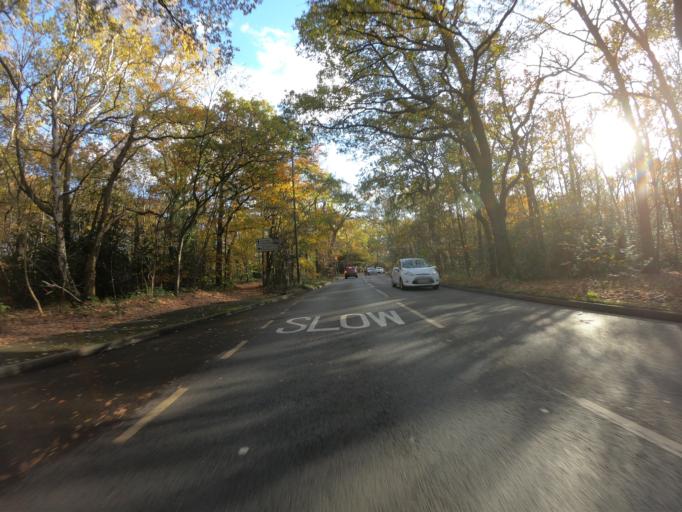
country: GB
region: England
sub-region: Greater London
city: Chislehurst
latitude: 51.4017
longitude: 0.0871
